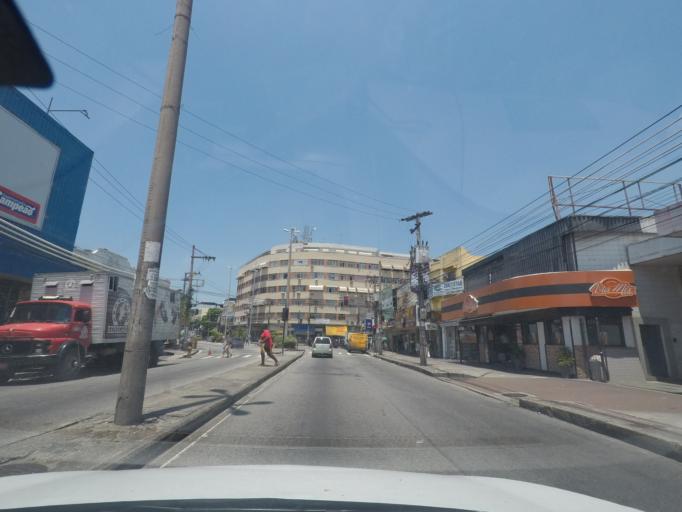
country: BR
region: Rio de Janeiro
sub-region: Rio De Janeiro
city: Rio de Janeiro
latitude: -22.8852
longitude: -43.2989
